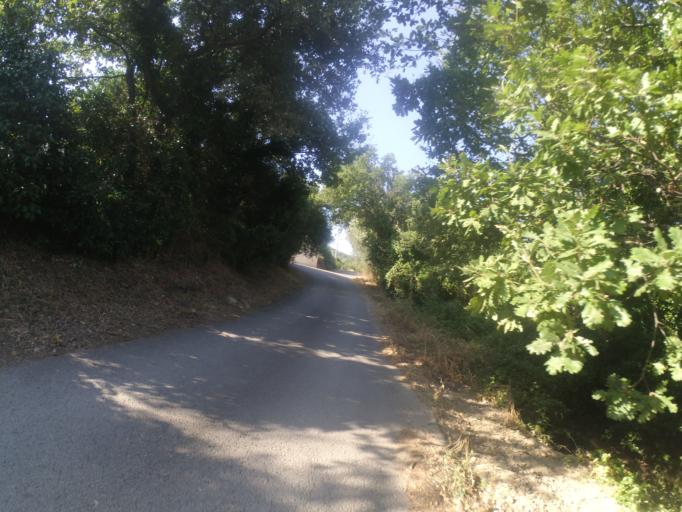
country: FR
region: Languedoc-Roussillon
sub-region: Departement des Pyrenees-Orientales
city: Ille-sur-Tet
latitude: 42.6534
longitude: 2.6571
